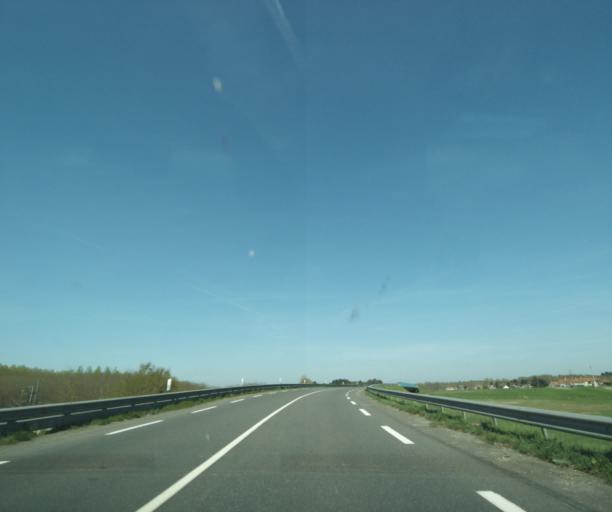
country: FR
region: Bourgogne
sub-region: Departement de la Nievre
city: Chantenay-Saint-Imbert
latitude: 46.6737
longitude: 3.2346
